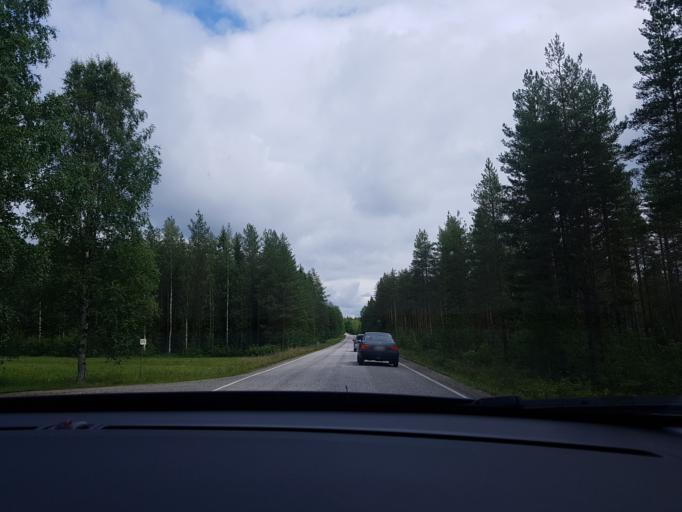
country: FI
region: Kainuu
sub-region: Kehys-Kainuu
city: Kuhmo
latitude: 64.1926
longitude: 29.4478
